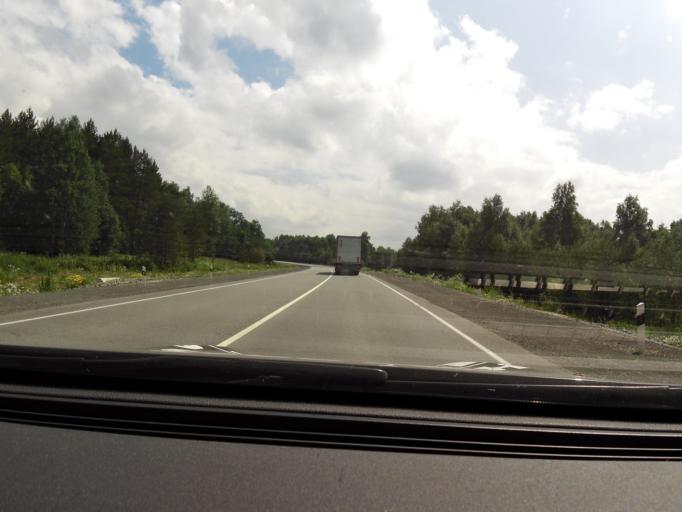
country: RU
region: Perm
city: Suksun
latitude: 56.9989
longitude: 57.4789
